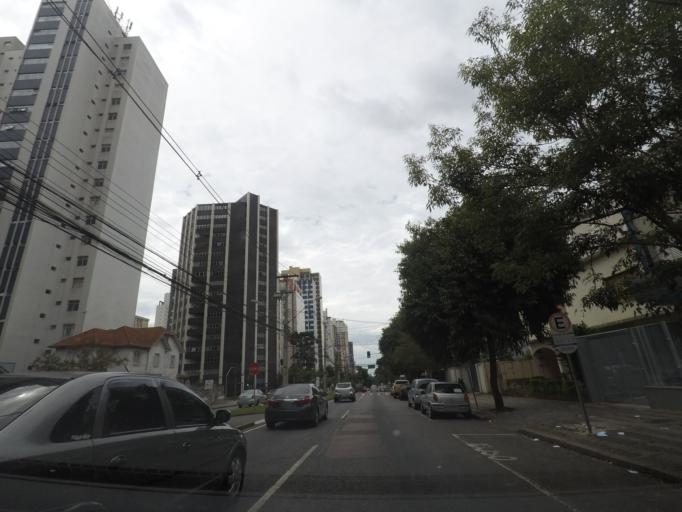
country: BR
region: Parana
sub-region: Curitiba
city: Curitiba
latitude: -25.4439
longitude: -49.2785
